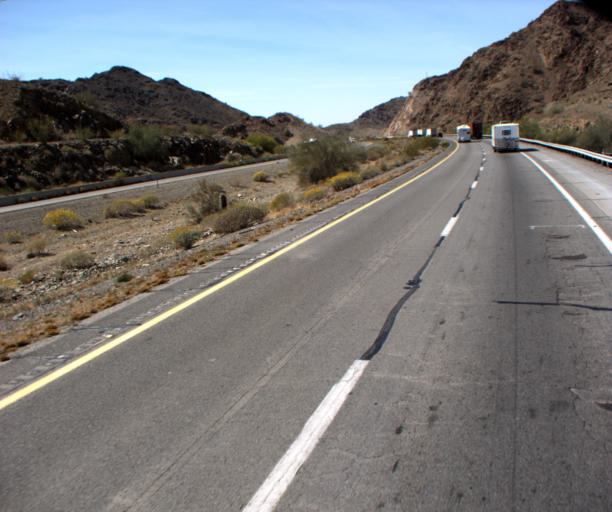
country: US
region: Arizona
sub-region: La Paz County
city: Quartzsite
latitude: 33.6481
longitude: -114.3724
